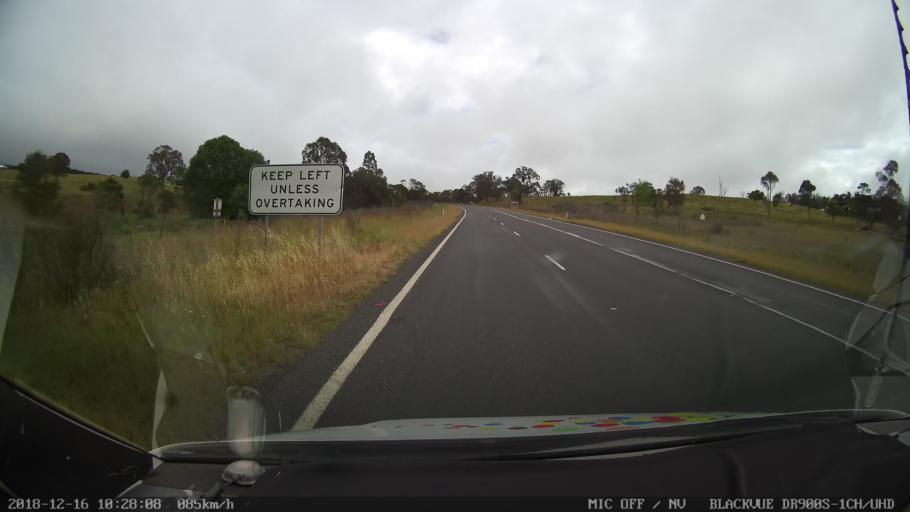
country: AU
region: New South Wales
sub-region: Tenterfield Municipality
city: Carrolls Creek
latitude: -29.1249
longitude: 151.9972
